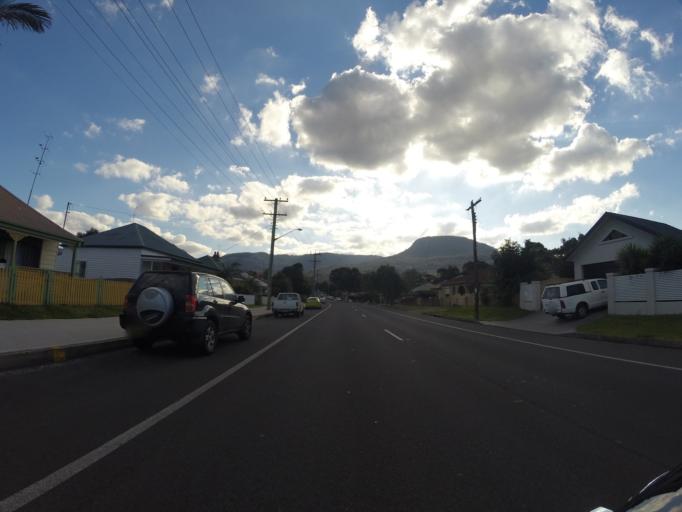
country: AU
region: New South Wales
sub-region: Wollongong
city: West Wollongong
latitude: -34.4214
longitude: 150.8645
